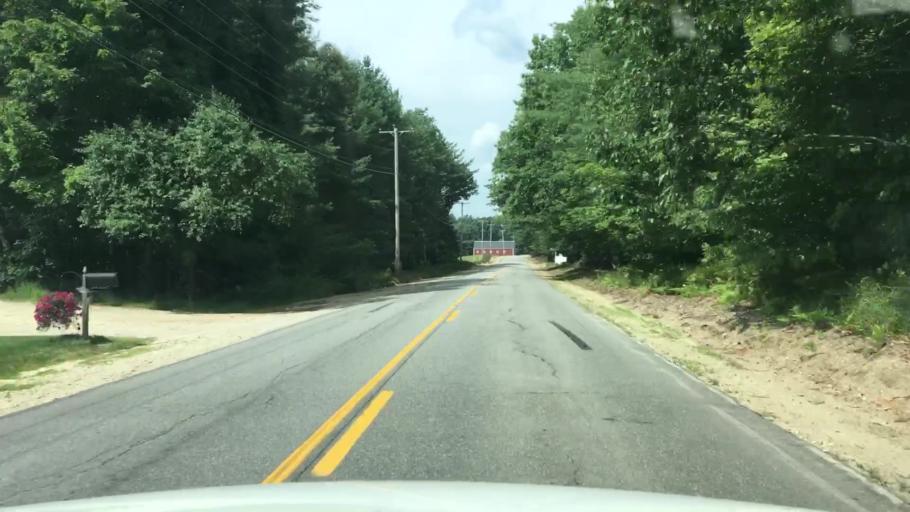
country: US
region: Maine
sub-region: Oxford County
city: Rumford
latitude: 44.5321
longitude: -70.6663
